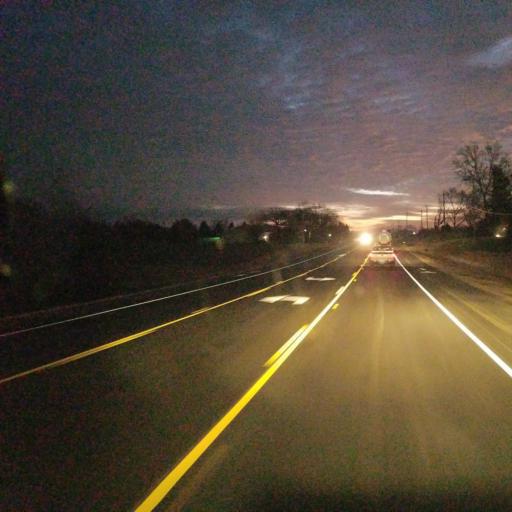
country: US
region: Illinois
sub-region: Peoria County
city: Hanna City
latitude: 40.6918
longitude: -89.7785
